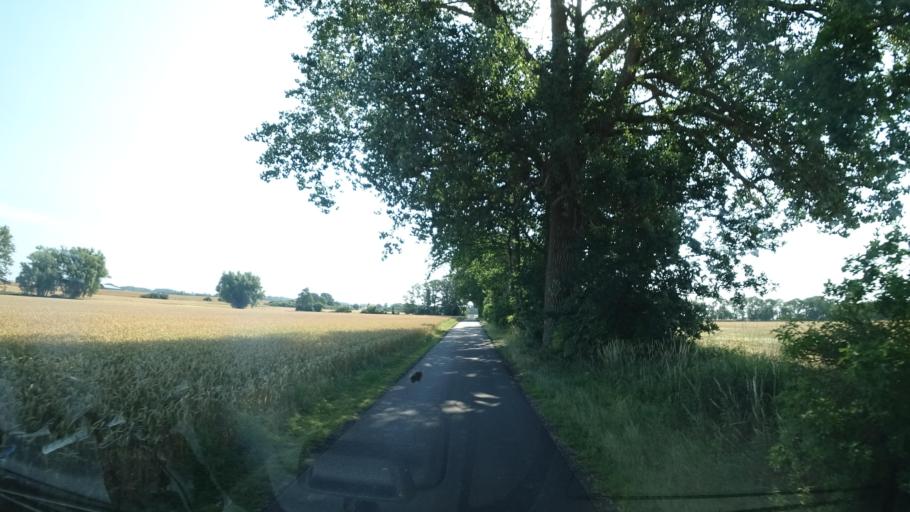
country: DE
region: Mecklenburg-Vorpommern
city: Kemnitz
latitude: 54.1209
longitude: 13.5544
